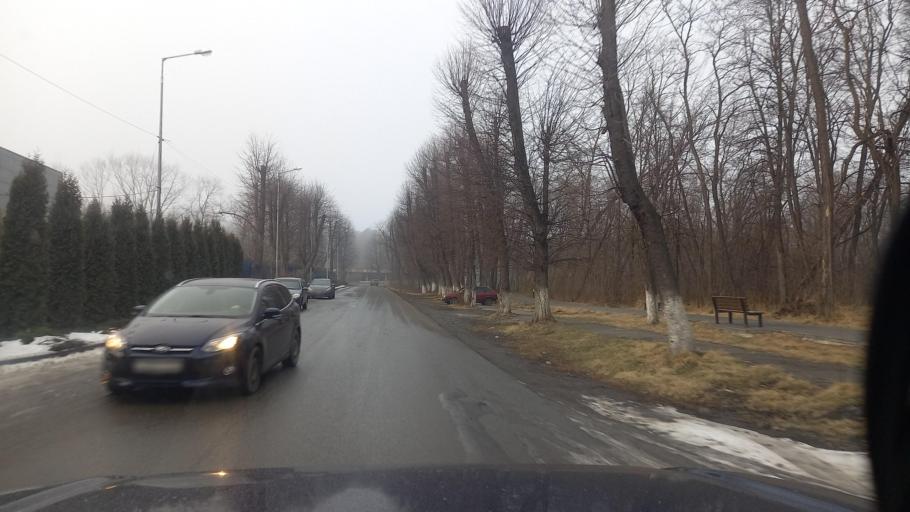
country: RU
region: North Ossetia
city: Vladikavkaz
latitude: 42.9877
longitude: 44.6771
